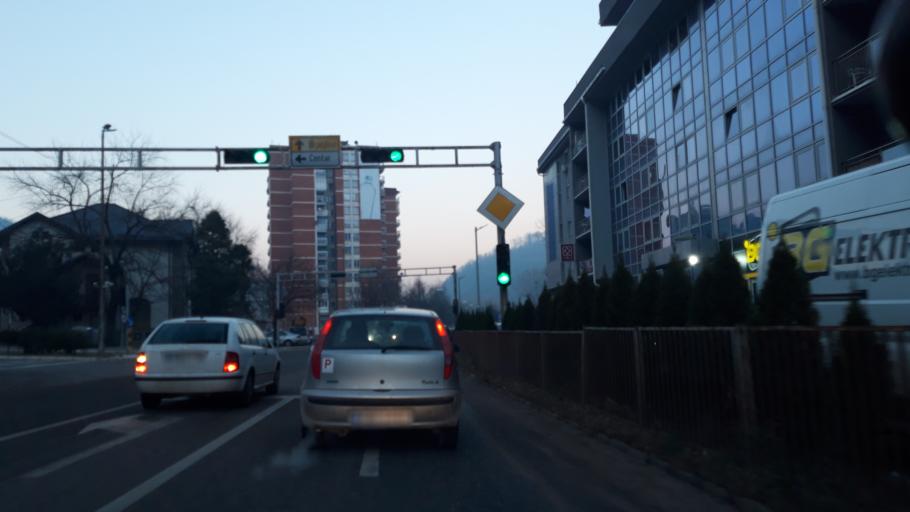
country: RS
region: Central Serbia
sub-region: Macvanski Okrug
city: Mali Zvornik
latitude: 44.3789
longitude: 19.1028
